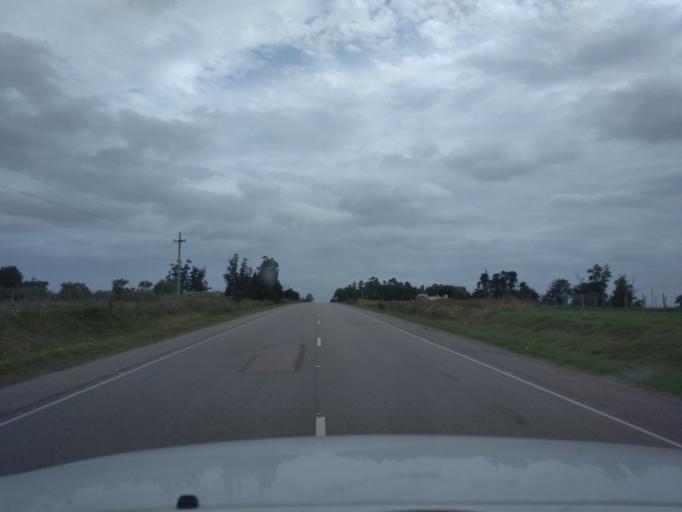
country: UY
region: Canelones
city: Tala
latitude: -34.3182
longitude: -55.7446
